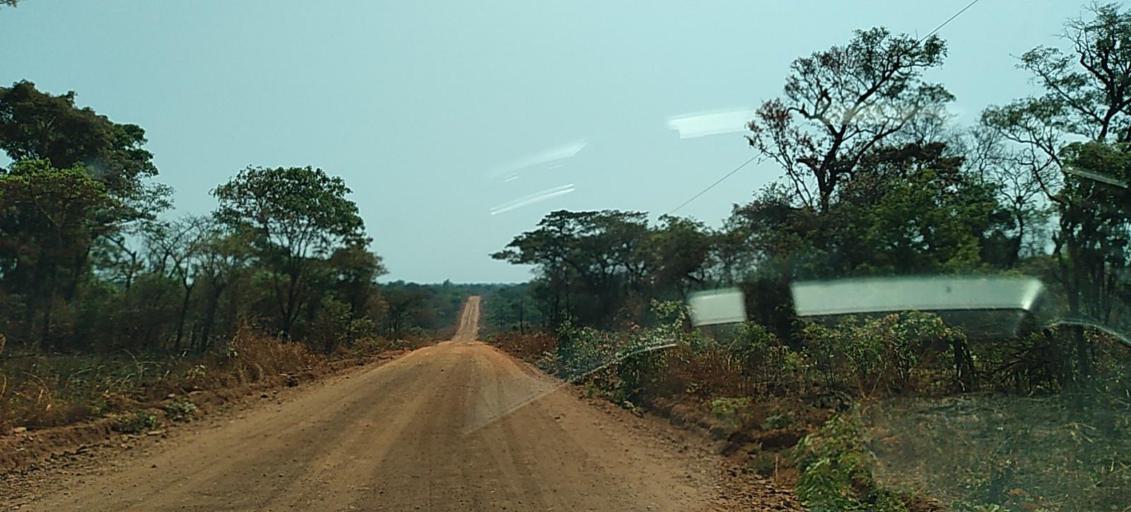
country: ZM
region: North-Western
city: Kansanshi
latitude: -12.0003
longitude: 26.5906
